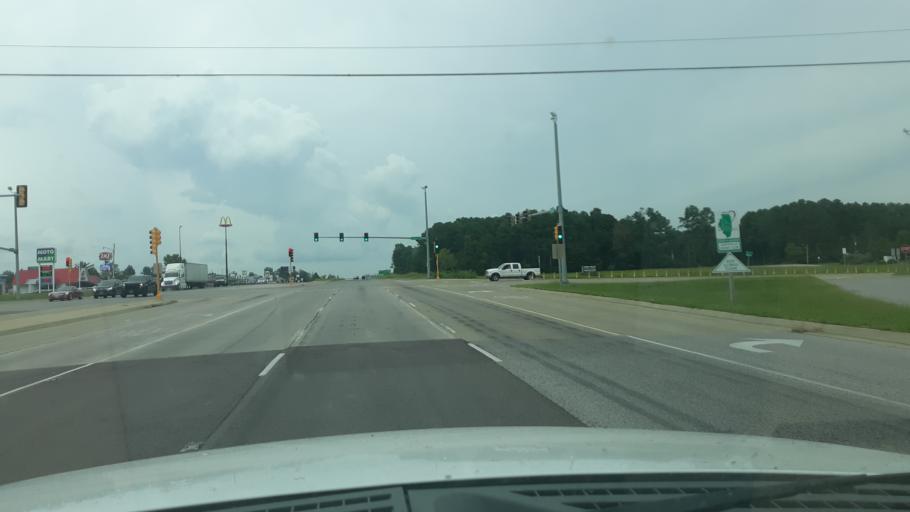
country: US
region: Illinois
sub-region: Williamson County
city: Crainville
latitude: 37.7450
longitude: -89.0783
